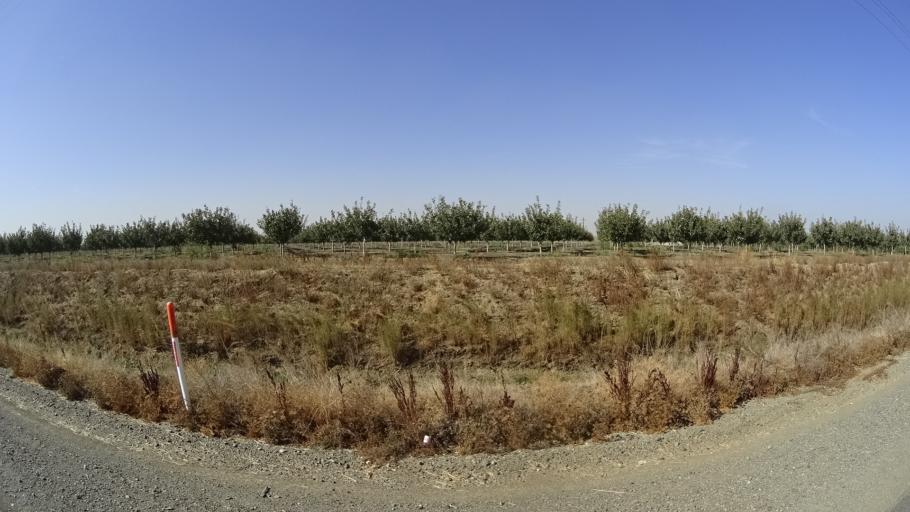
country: US
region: California
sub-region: Yolo County
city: Davis
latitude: 38.5048
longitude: -121.6955
